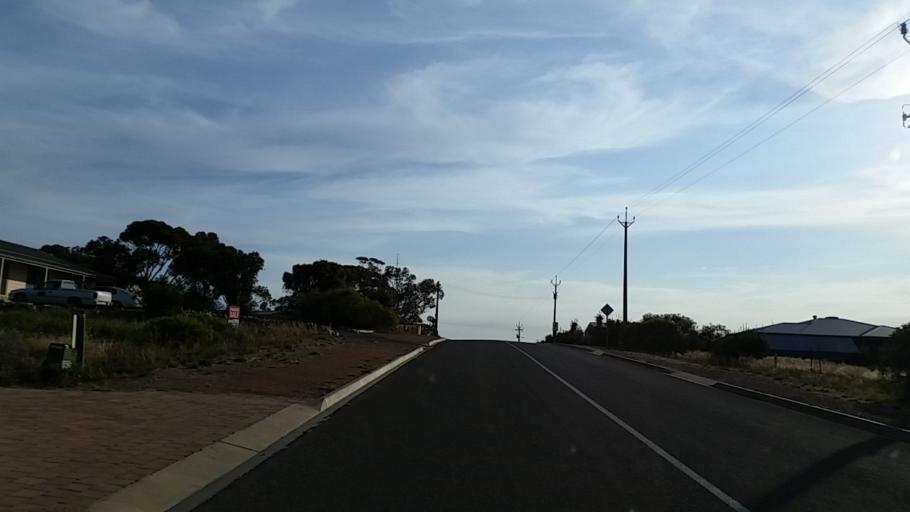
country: AU
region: South Australia
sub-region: Port Pirie City and Dists
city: Port Pirie
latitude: -33.1036
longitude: 138.0300
